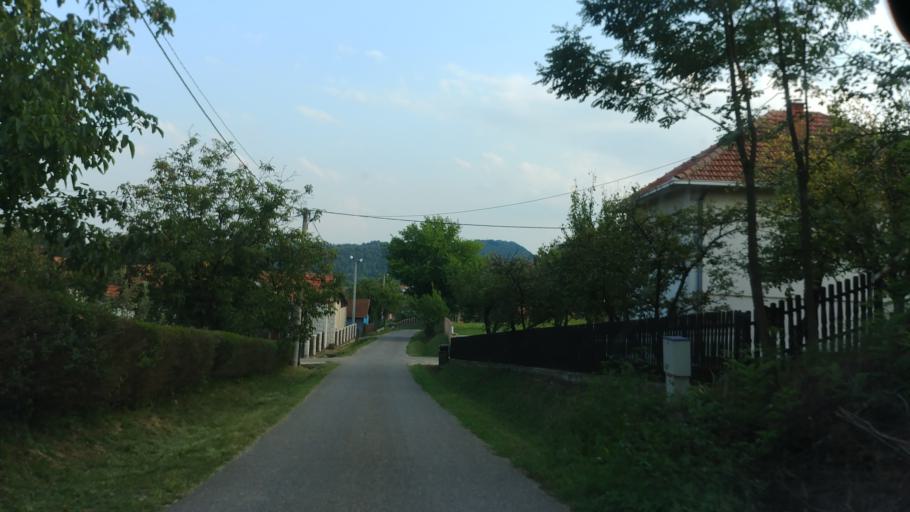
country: BA
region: Republika Srpska
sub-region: Opstina Ugljevik
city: Ugljevik
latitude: 44.7000
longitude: 19.0107
